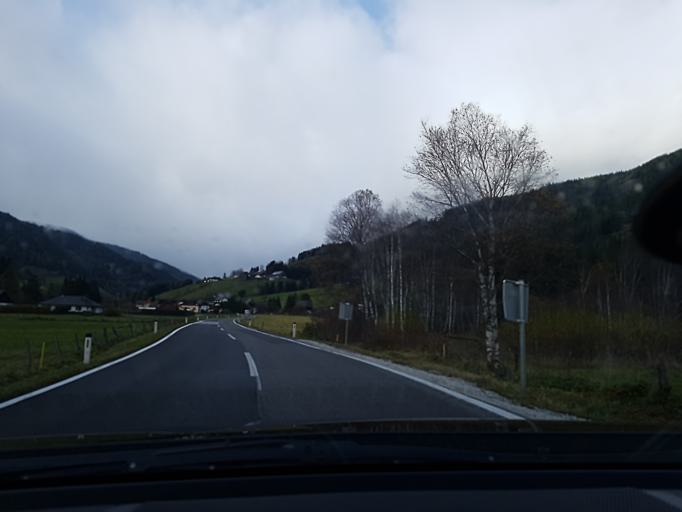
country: AT
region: Styria
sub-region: Politischer Bezirk Murtal
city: Sankt Johann am Tauern
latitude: 47.3153
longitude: 14.4823
